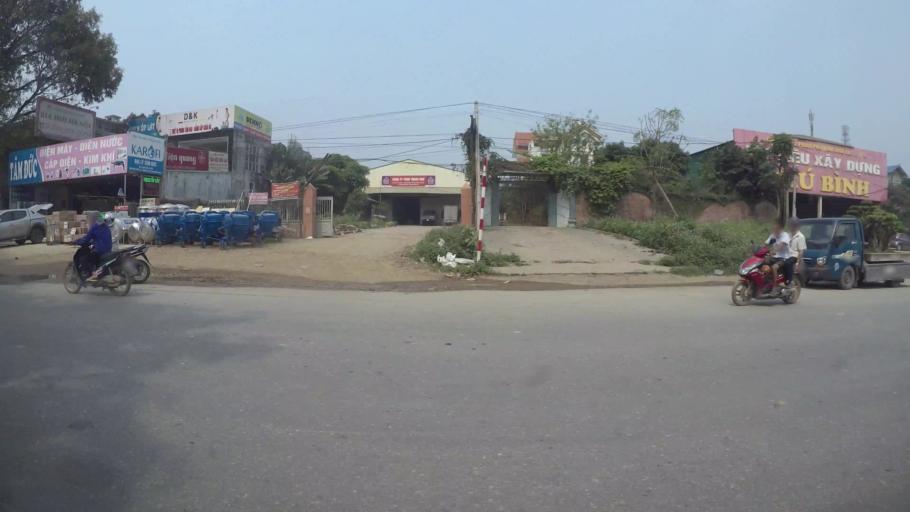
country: VN
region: Ha Noi
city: Lien Quan
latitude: 20.9850
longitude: 105.5265
